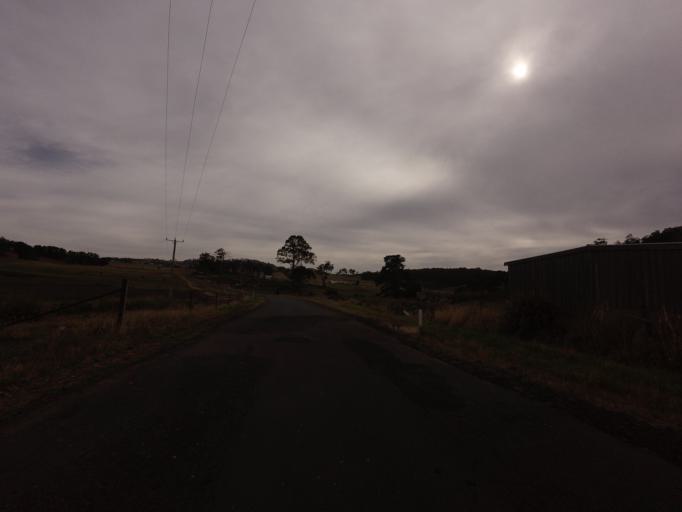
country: AU
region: Tasmania
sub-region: Sorell
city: Sorell
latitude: -42.4619
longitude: 147.5725
